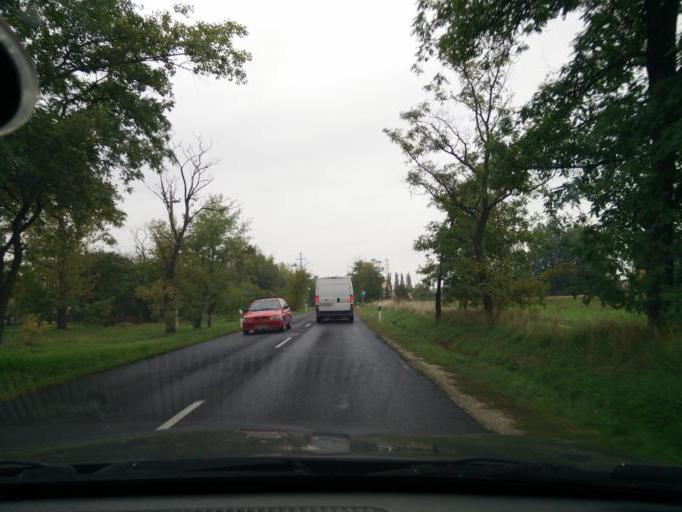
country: HU
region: Komarom-Esztergom
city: Tat
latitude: 47.7358
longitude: 18.6507
